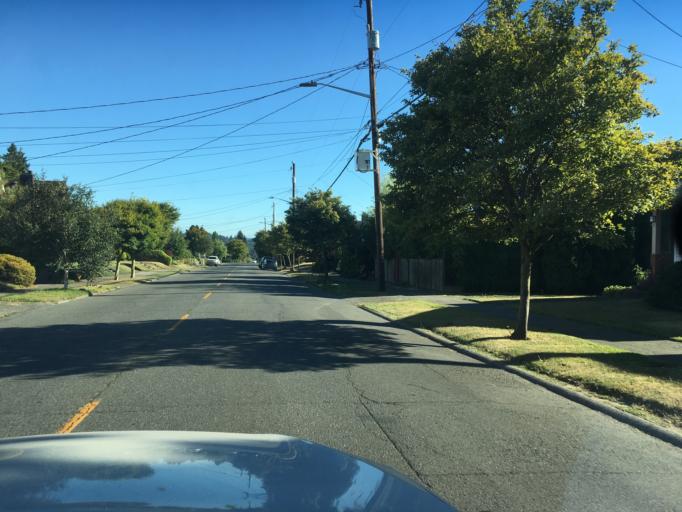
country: US
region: Washington
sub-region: King County
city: Shoreline
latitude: 47.6848
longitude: -122.3983
